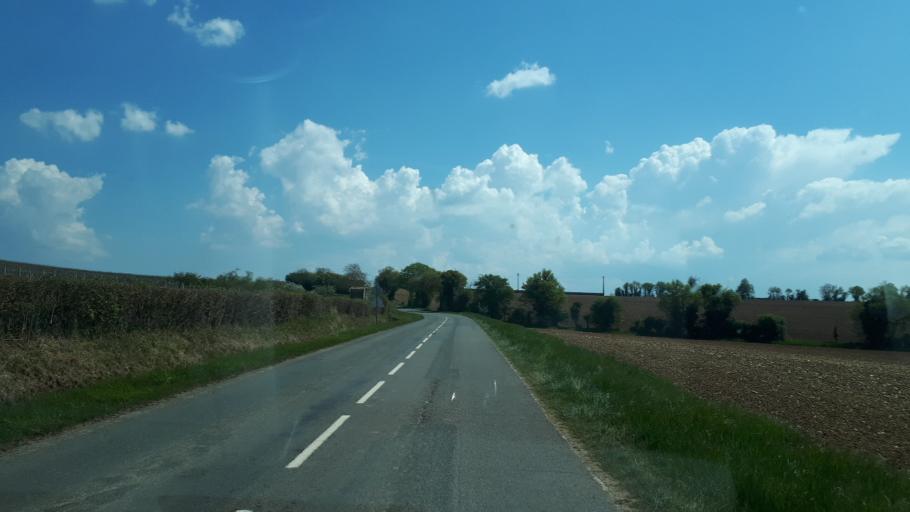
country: FR
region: Centre
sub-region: Departement du Cher
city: Sancerre
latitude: 47.3045
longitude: 2.7334
